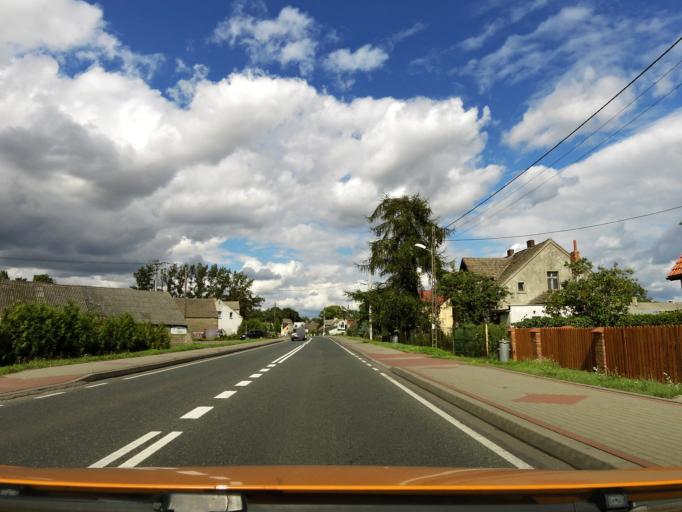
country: PL
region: West Pomeranian Voivodeship
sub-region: Powiat goleniowski
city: Nowogard
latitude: 53.7170
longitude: 15.1881
